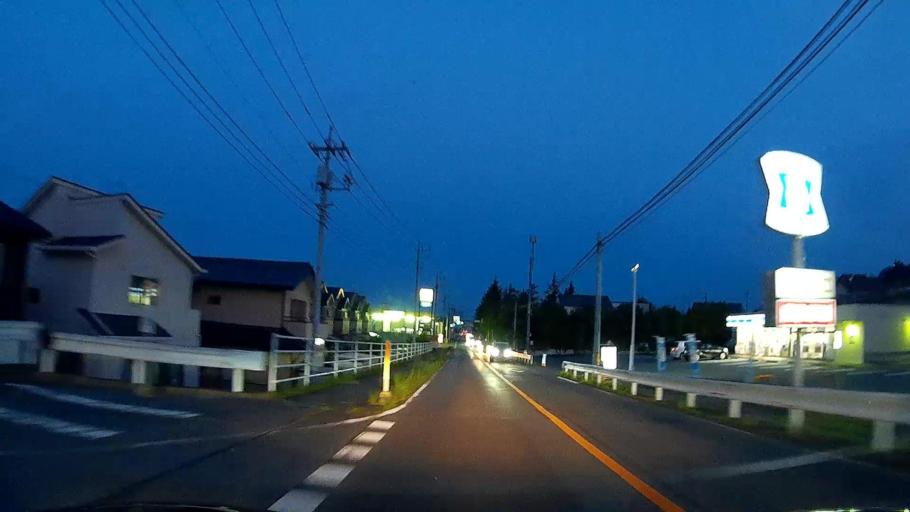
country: JP
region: Gunma
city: Takasaki
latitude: 36.3374
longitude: 138.9796
